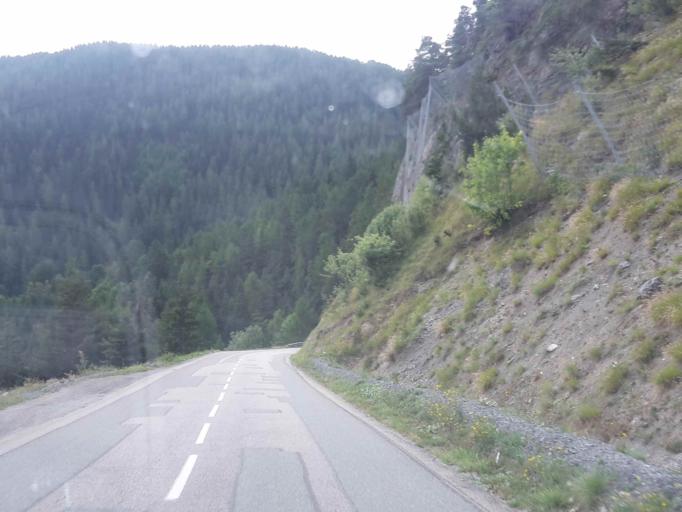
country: FR
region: Rhone-Alpes
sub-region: Departement de la Savoie
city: Saint-Michel-de-Maurienne
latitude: 45.1985
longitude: 6.4456
